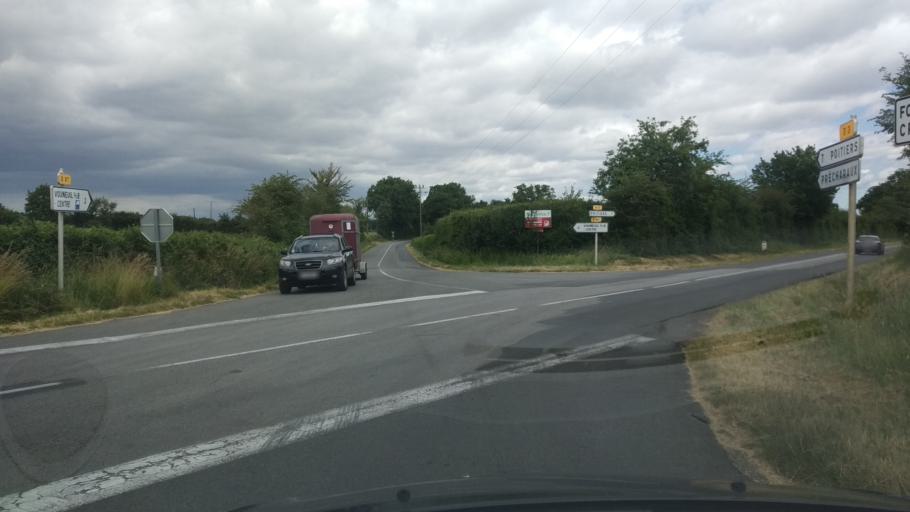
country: FR
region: Poitou-Charentes
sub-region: Departement de la Vienne
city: Vouneuil-sous-Biard
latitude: 46.5588
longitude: 0.2627
